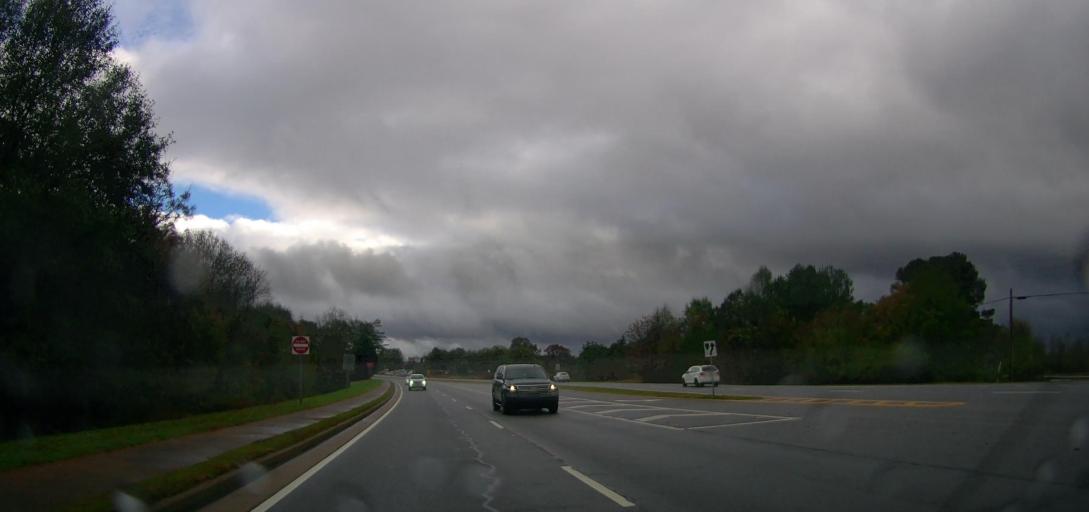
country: US
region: Georgia
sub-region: Jackson County
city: Nicholson
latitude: 34.1021
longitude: -83.4332
